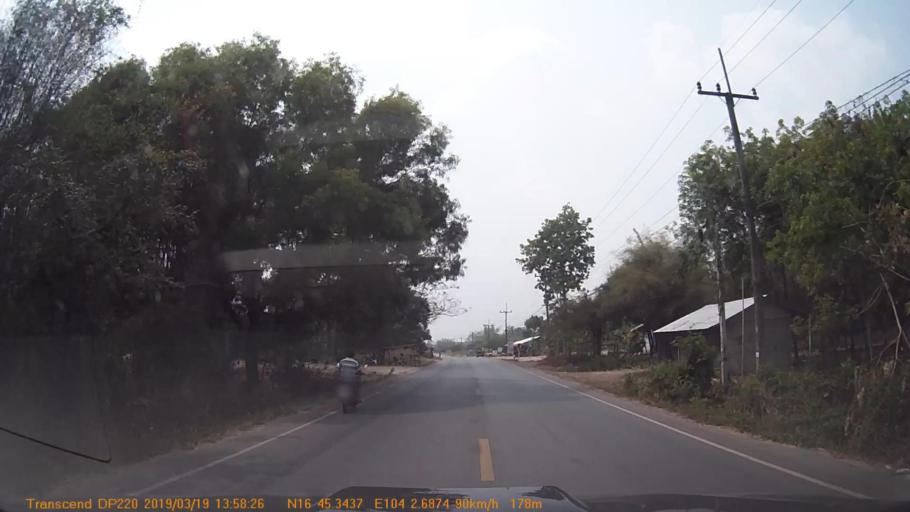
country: TH
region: Kalasin
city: Na Khu
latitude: 16.7559
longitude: 104.0444
